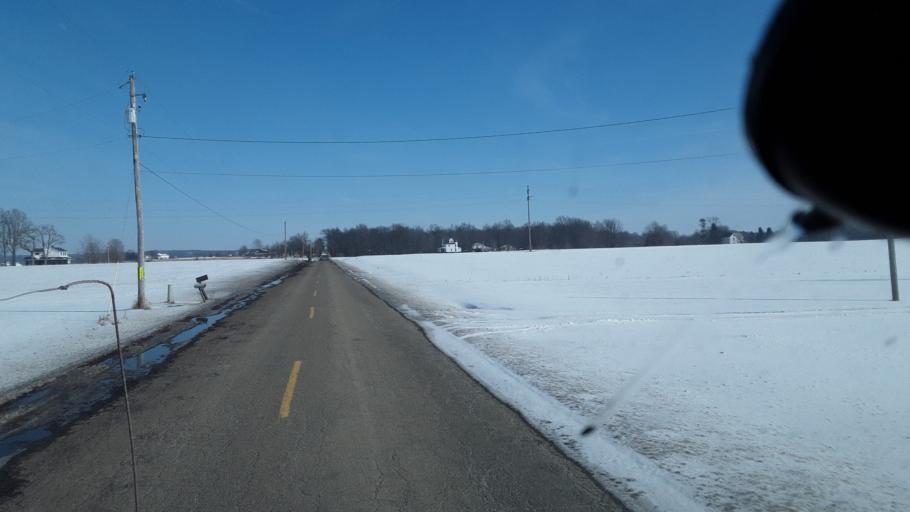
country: US
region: Ohio
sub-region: Mahoning County
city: Sebring
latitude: 40.9594
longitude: -80.9865
